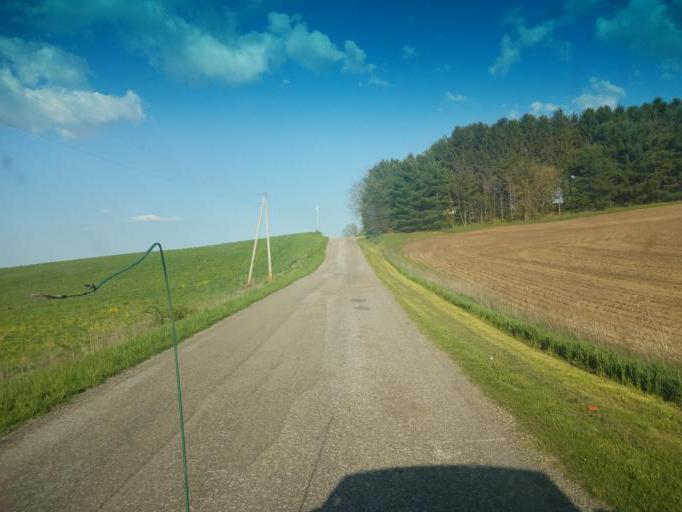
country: US
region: Ohio
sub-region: Wayne County
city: Shreve
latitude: 40.5950
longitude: -82.0609
